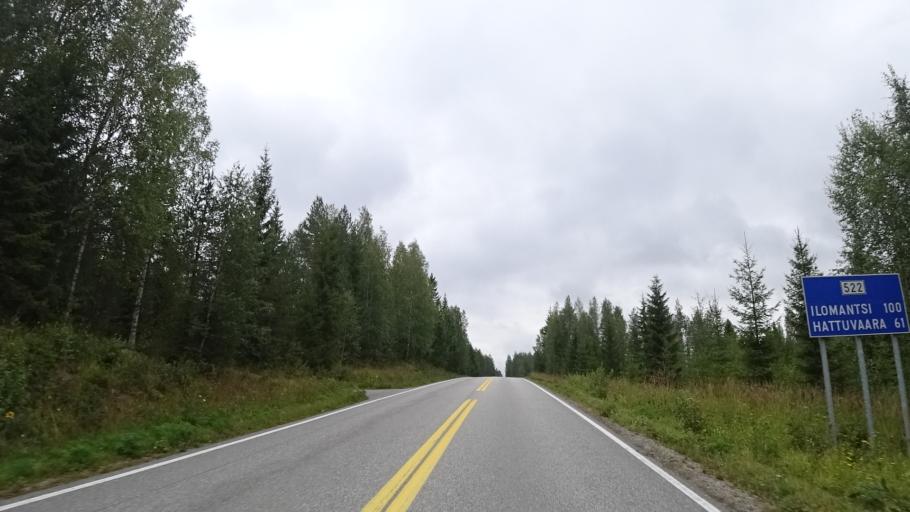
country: FI
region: North Karelia
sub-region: Pielisen Karjala
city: Lieksa
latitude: 63.2801
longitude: 30.5921
